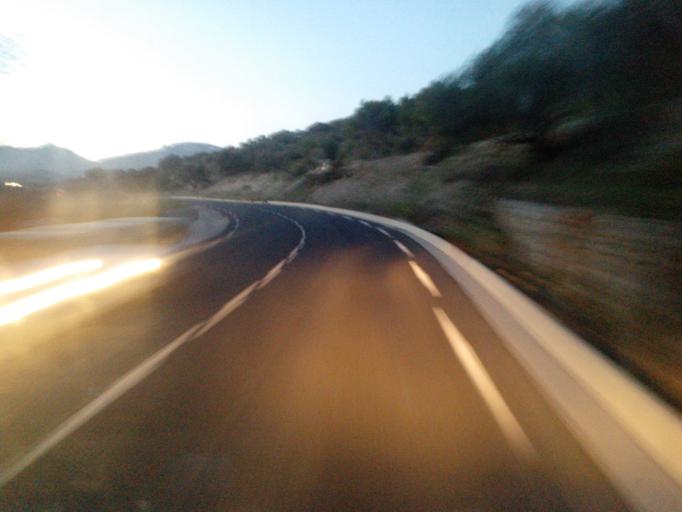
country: FR
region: Languedoc-Roussillon
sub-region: Departement des Pyrenees-Orientales
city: Estagel
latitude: 42.7811
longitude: 2.6899
